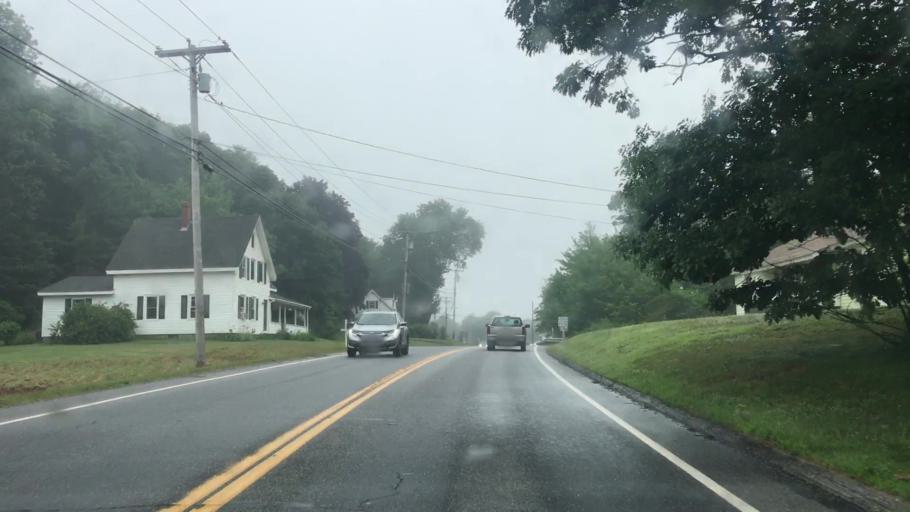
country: US
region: Maine
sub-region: Lincoln County
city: Boothbay
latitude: 43.8814
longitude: -69.6321
